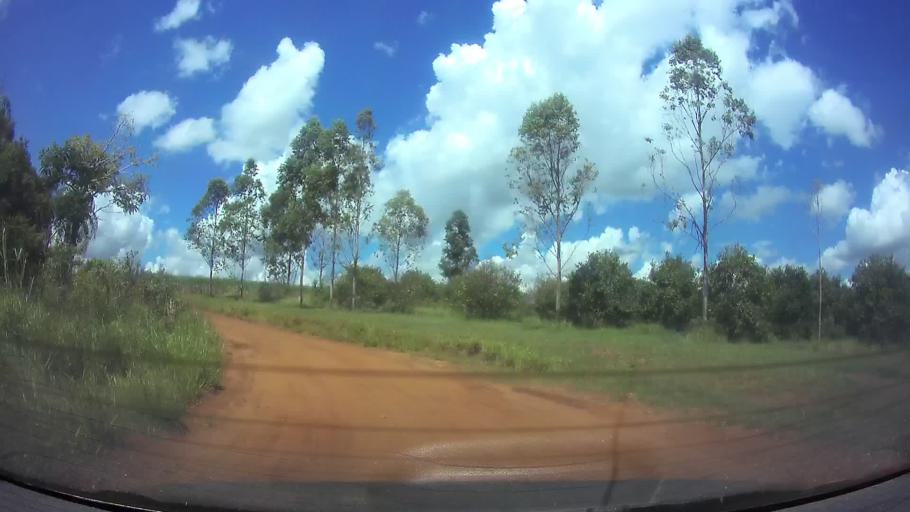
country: PY
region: Paraguari
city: La Colmena
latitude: -25.9544
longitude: -56.7694
